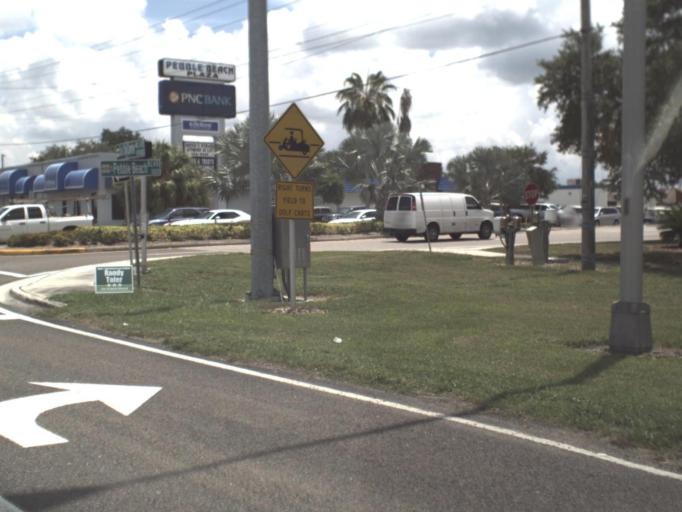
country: US
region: Florida
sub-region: Hillsborough County
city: Sun City Center
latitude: 27.7122
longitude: -82.3523
